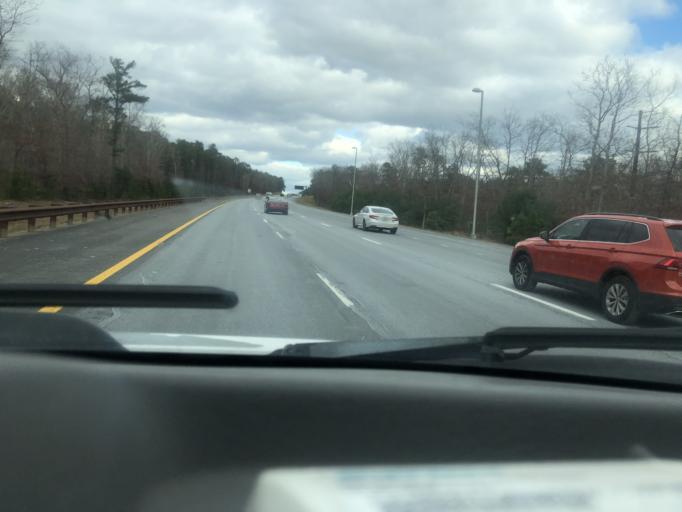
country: US
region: New Jersey
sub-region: Ocean County
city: Manahawkin
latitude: 39.7159
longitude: -74.2755
